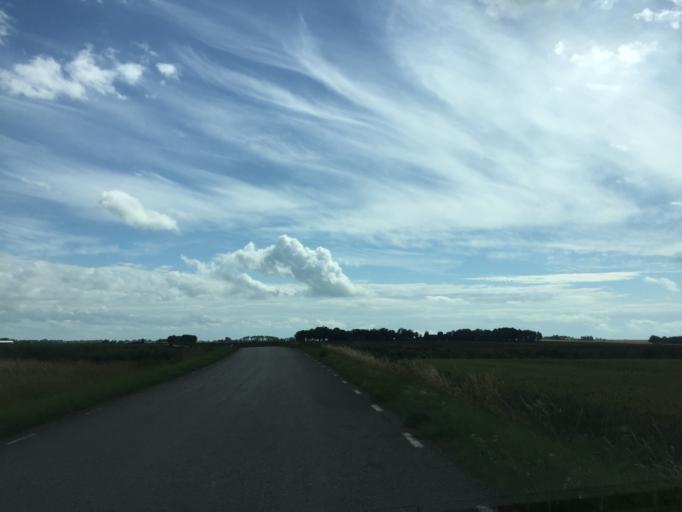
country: SE
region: OEstergoetland
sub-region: Vadstena Kommun
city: Vadstena
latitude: 58.4522
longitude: 14.8376
